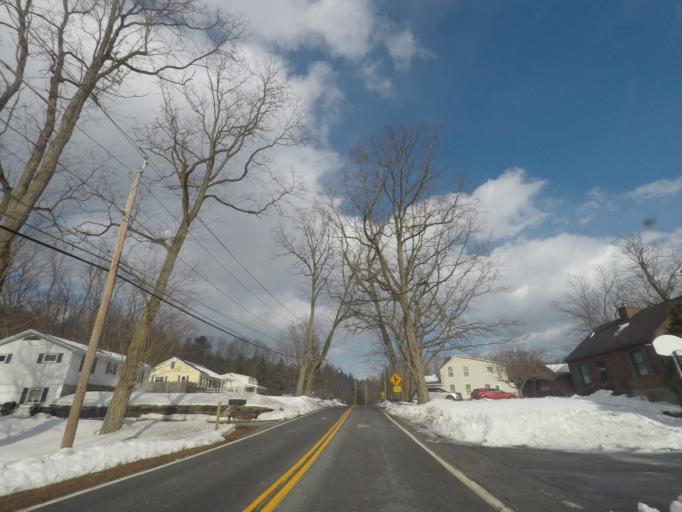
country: US
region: New York
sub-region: Albany County
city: Cohoes
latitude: 42.8151
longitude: -73.7482
